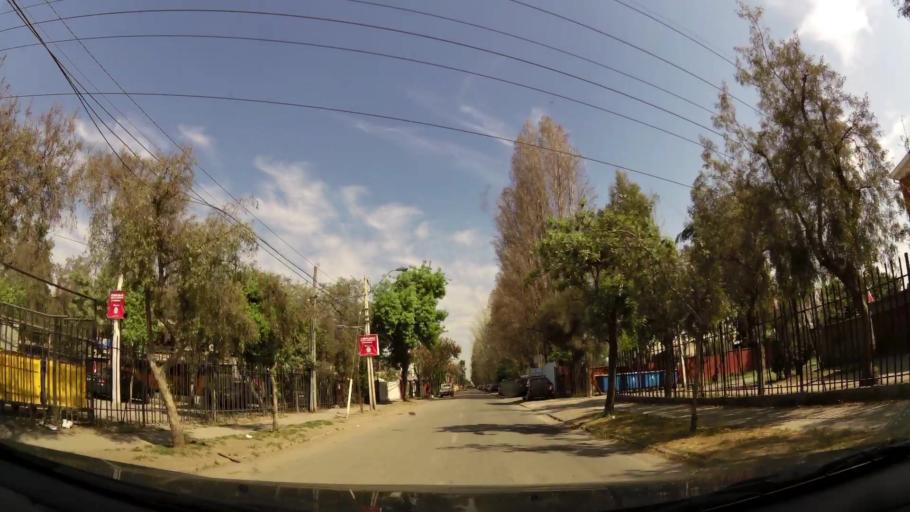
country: CL
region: Santiago Metropolitan
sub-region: Provincia de Santiago
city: La Pintana
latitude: -33.5653
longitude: -70.5992
